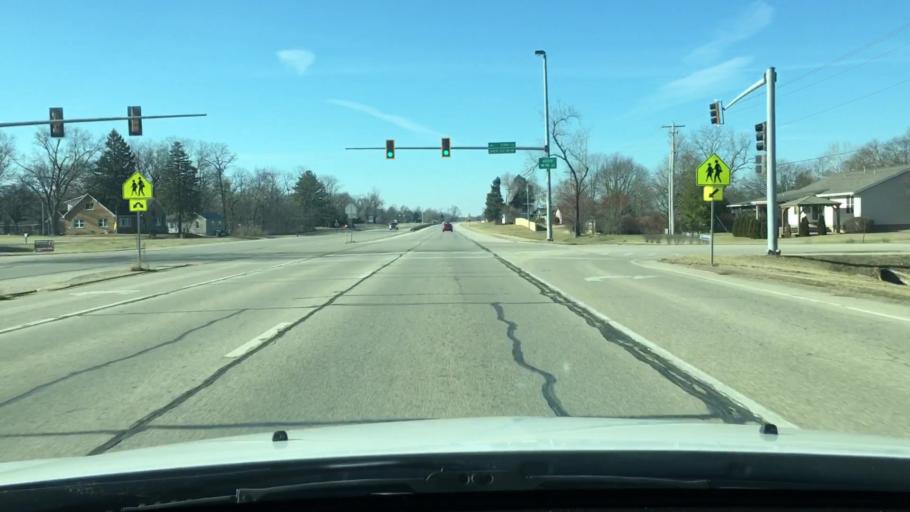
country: US
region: Illinois
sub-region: Woodford County
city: Germantown Hills
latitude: 40.7696
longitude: -89.4518
